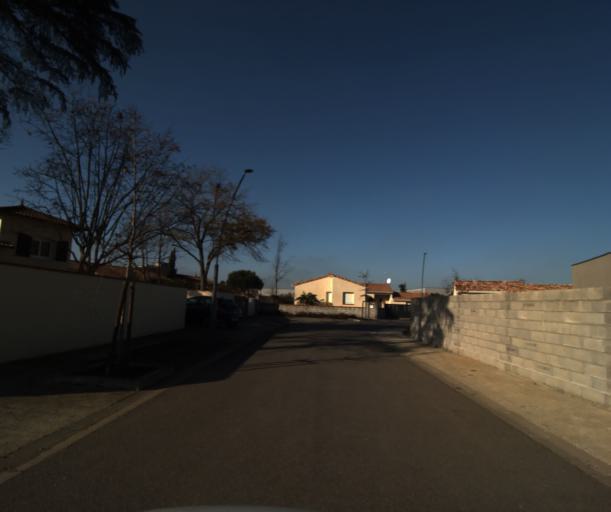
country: FR
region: Midi-Pyrenees
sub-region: Departement de la Haute-Garonne
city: Colomiers
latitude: 43.5952
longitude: 1.3583
